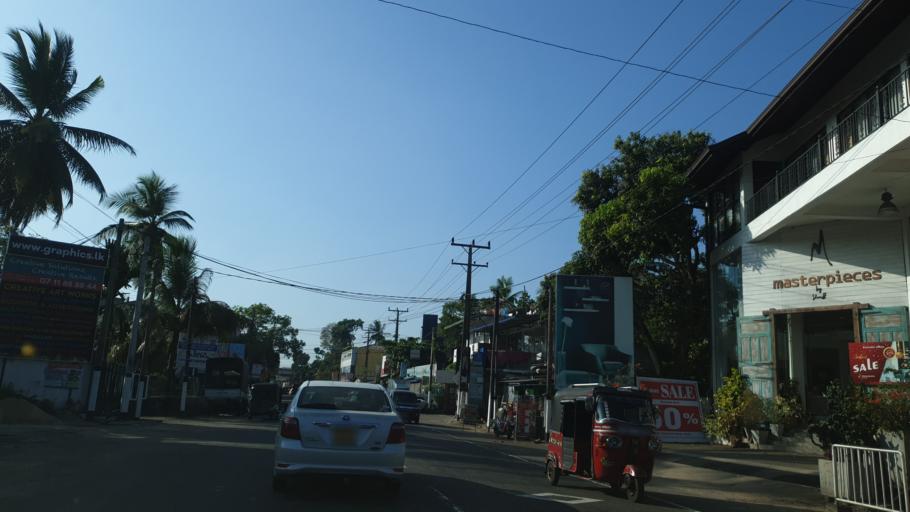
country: LK
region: Western
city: Sri Jayewardenepura Kotte
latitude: 6.8773
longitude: 79.9256
